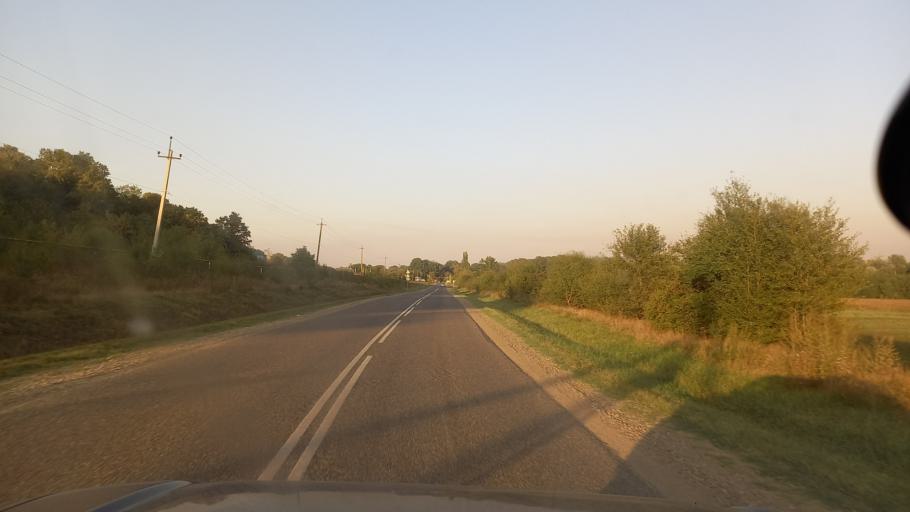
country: RU
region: Krasnodarskiy
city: Smolenskaya
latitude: 44.7618
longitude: 38.7698
